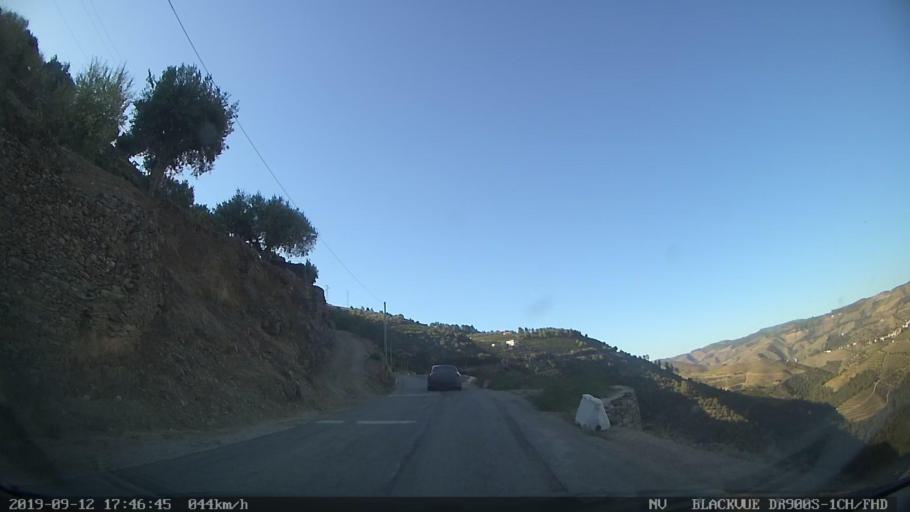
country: PT
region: Vila Real
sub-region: Sabrosa
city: Vilela
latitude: 41.2084
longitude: -7.5530
